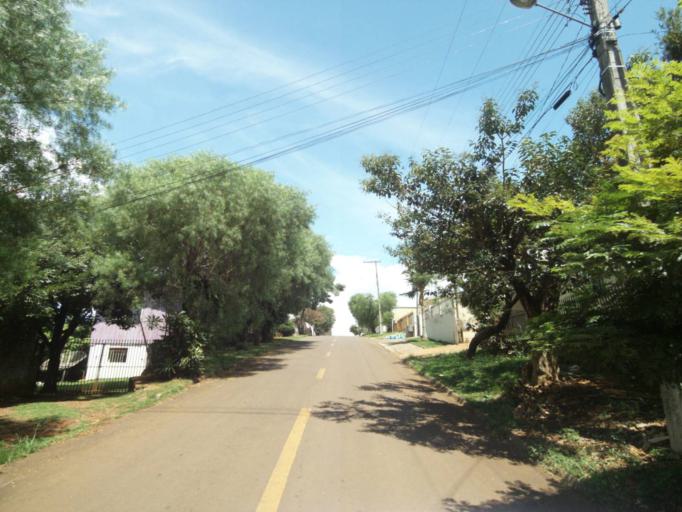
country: BR
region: Parana
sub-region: Guaraniacu
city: Guaraniacu
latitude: -25.0961
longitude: -52.8705
